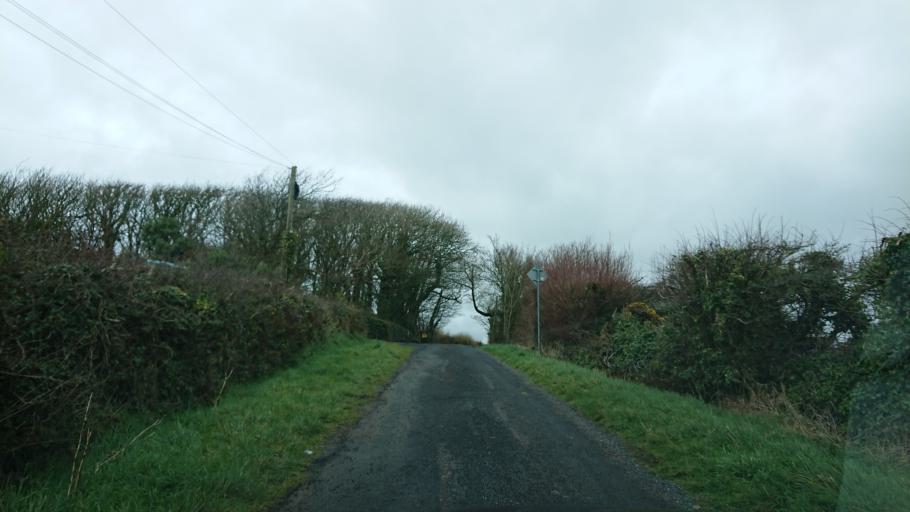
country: IE
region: Munster
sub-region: Waterford
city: Dunmore East
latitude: 52.1436
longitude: -7.0400
